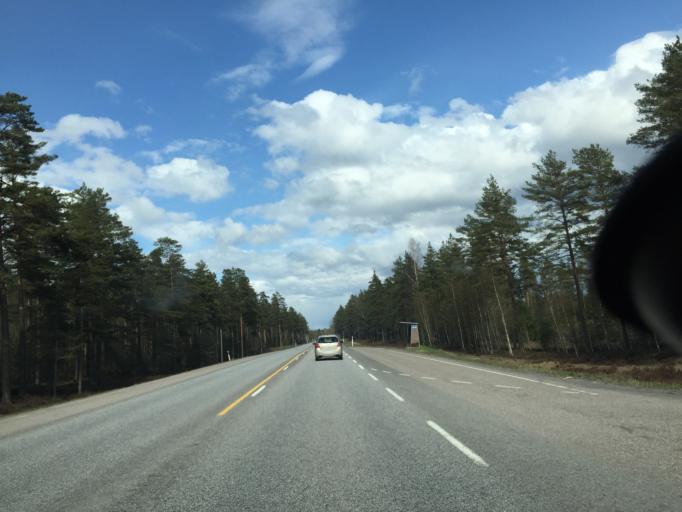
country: FI
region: Uusimaa
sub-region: Raaseporin
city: Pohja
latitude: 60.0266
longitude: 23.5834
